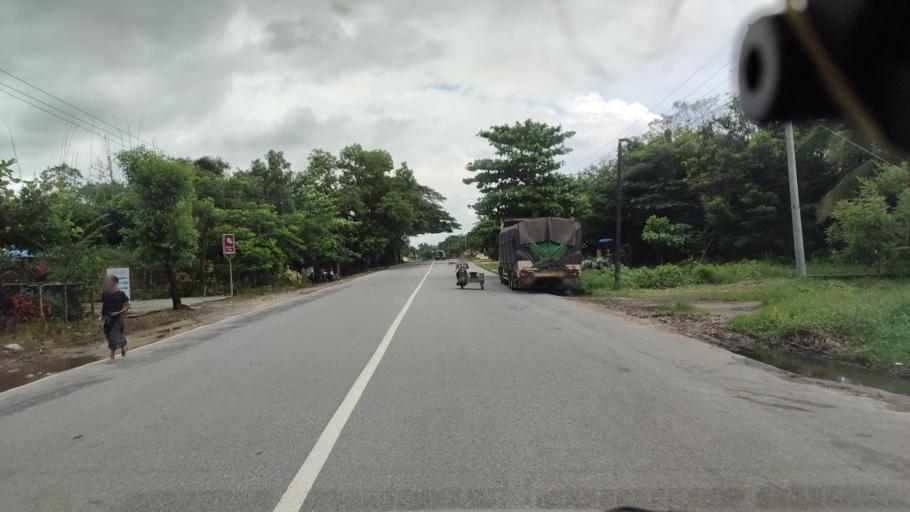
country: MM
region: Bago
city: Bago
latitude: 17.5762
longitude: 96.5546
